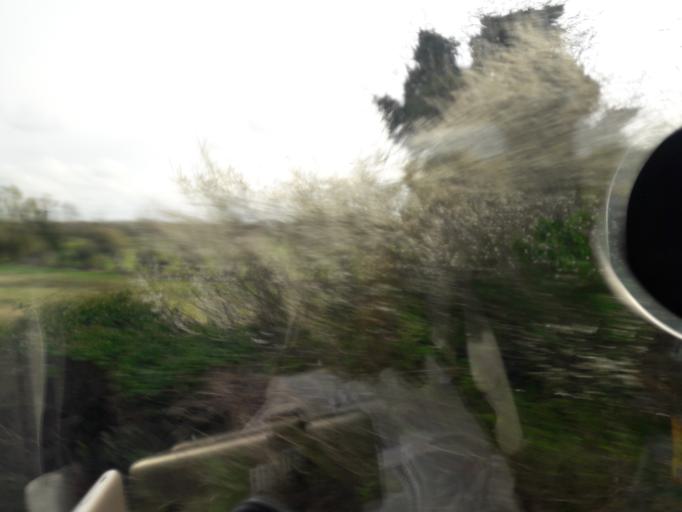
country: IE
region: Leinster
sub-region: An Mhi
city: Longwood
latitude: 53.4659
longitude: -6.9768
